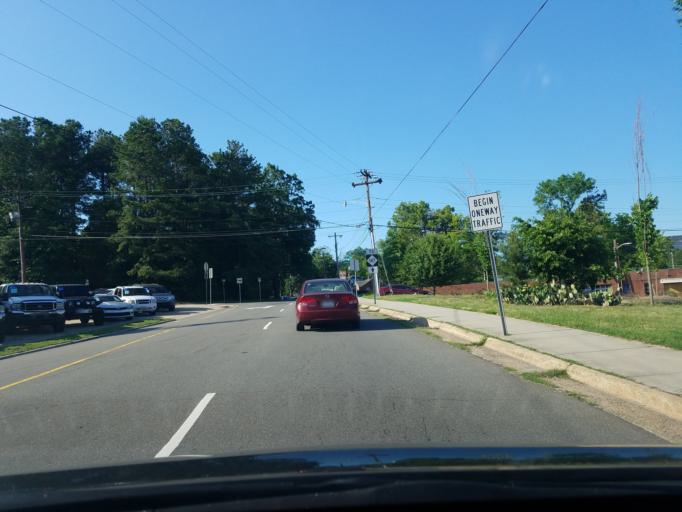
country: US
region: North Carolina
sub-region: Durham County
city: Durham
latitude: 35.9864
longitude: -78.9094
